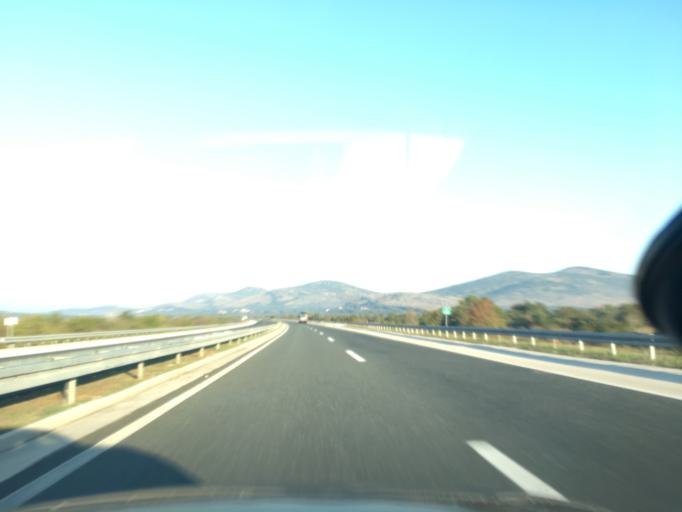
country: HR
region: Splitsko-Dalmatinska
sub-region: Grad Trogir
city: Trogir
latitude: 43.6734
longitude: 16.1587
